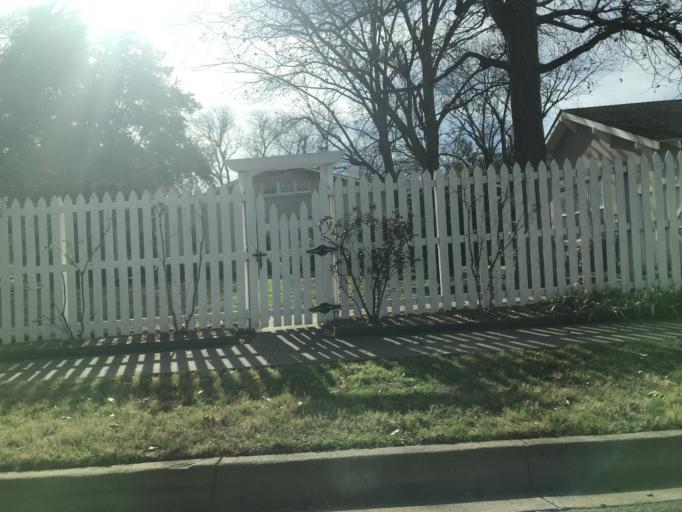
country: US
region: Texas
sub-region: Taylor County
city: Abilene
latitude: 32.4443
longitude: -99.7470
